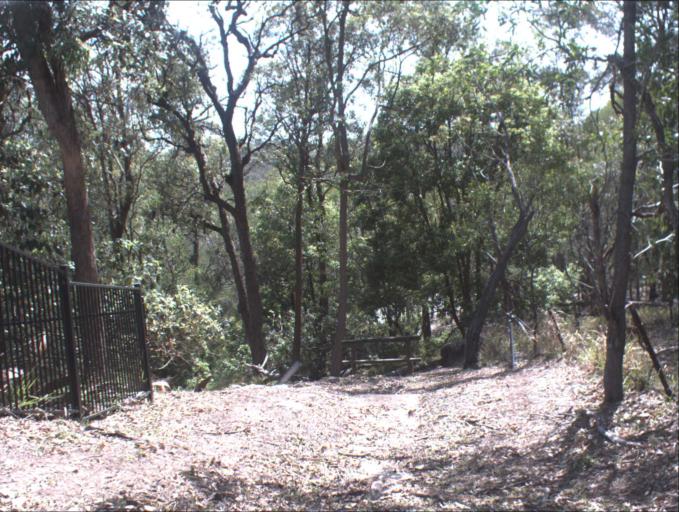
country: AU
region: Queensland
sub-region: Logan
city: Springwood
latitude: -27.6204
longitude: 153.1461
